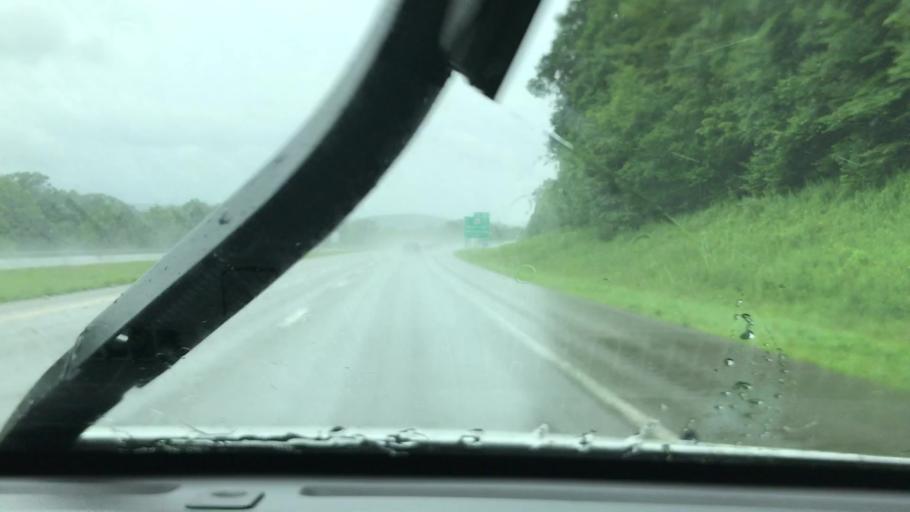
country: US
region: Pennsylvania
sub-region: Blair County
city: Tyrone
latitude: 40.6972
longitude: -78.2154
